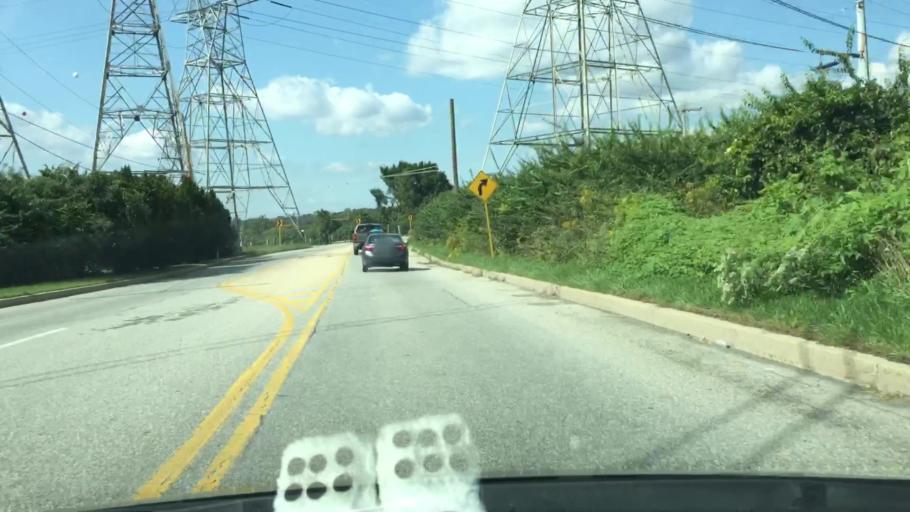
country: US
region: Pennsylvania
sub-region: Montgomery County
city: Plymouth Meeting
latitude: 40.1050
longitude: -75.2982
